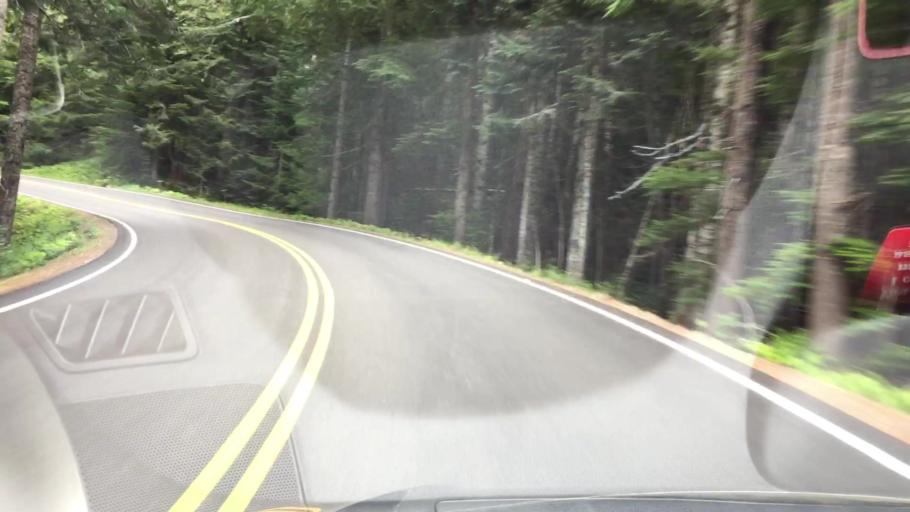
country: US
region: Washington
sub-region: Pierce County
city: Buckley
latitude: 46.7779
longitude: -121.7825
